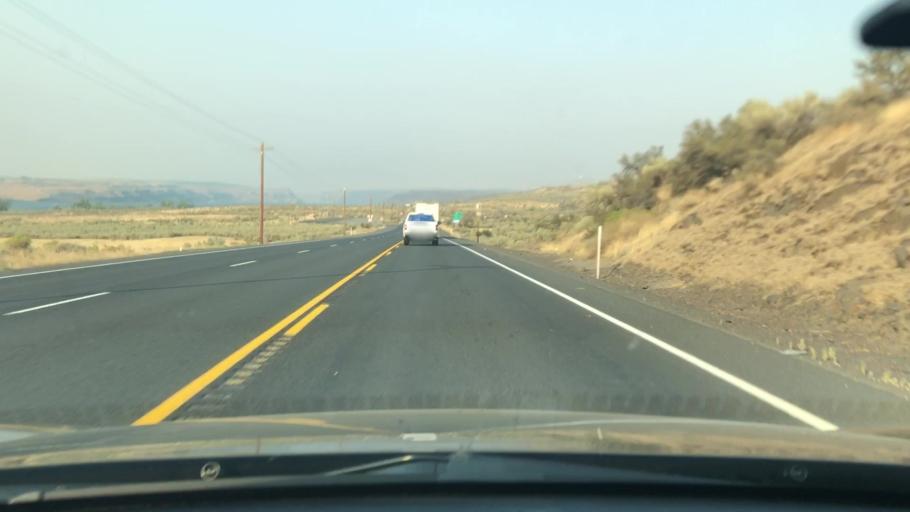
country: US
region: Oregon
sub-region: Umatilla County
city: Stanfield
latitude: 45.9121
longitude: -119.1427
